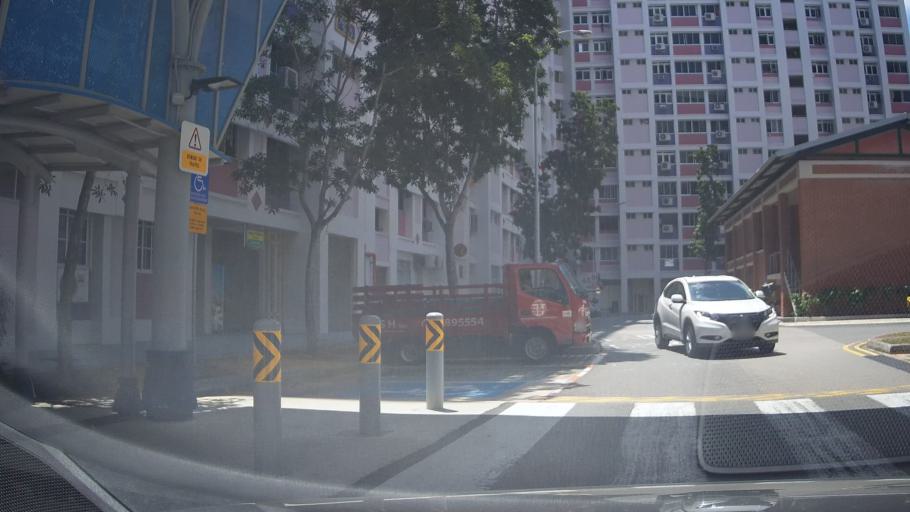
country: MY
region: Johor
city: Kampung Pasir Gudang Baru
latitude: 1.3743
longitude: 103.9605
